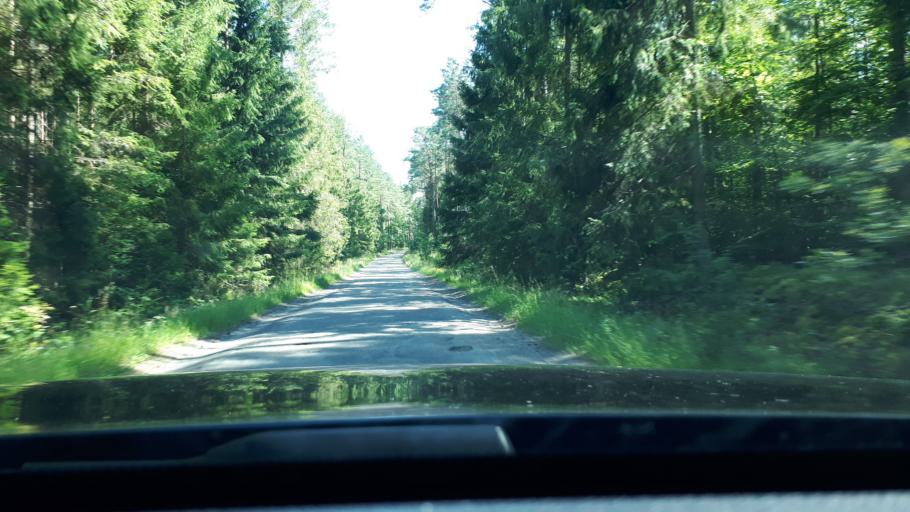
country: PL
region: Warmian-Masurian Voivodeship
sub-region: Powiat olsztynski
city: Stawiguda
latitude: 53.5849
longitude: 20.4507
